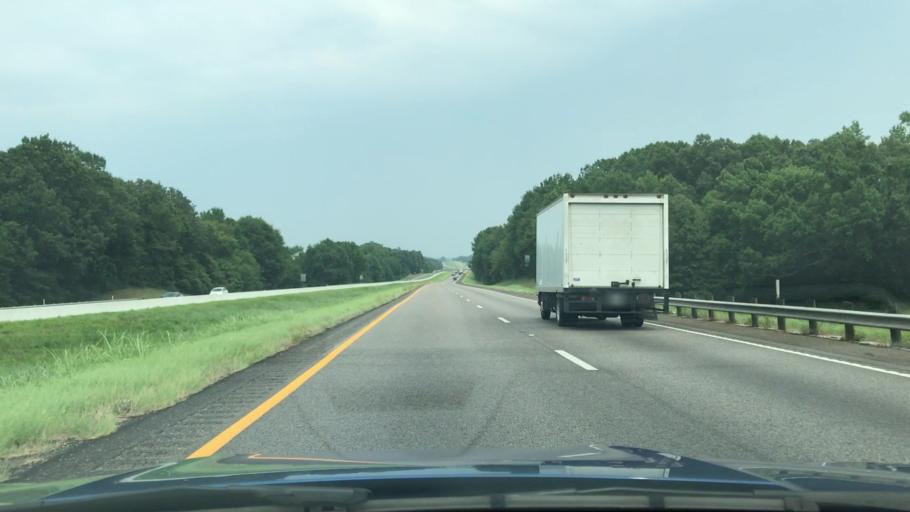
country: US
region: Texas
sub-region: Smith County
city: Tyler
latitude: 32.4522
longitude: -95.2456
